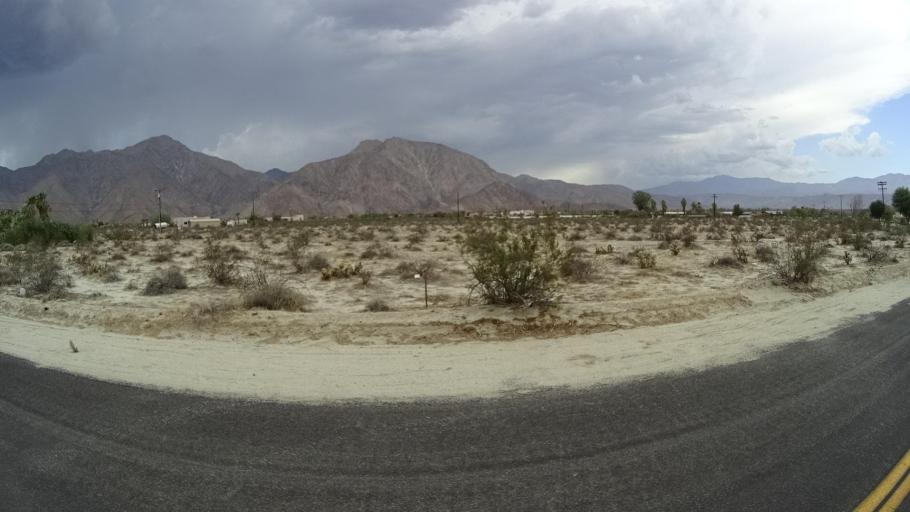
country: US
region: California
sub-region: San Diego County
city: Borrego Springs
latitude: 33.2637
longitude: -116.3844
